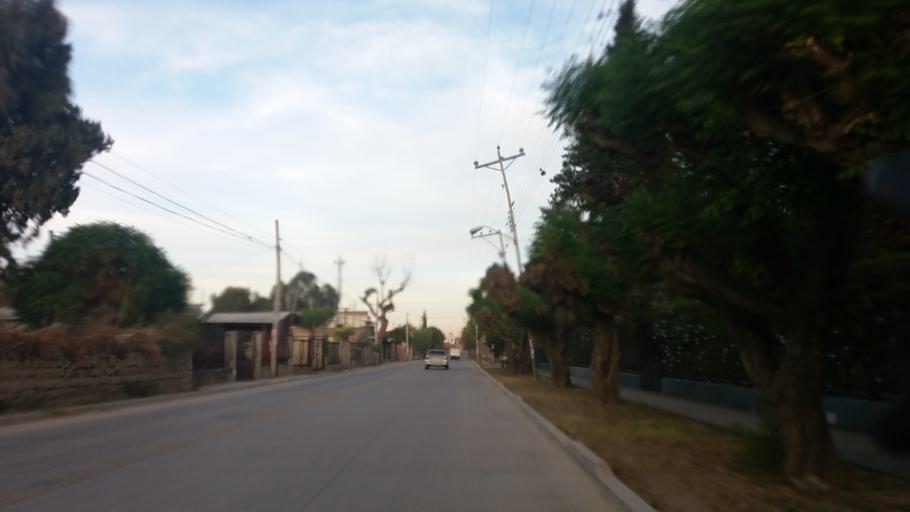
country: BO
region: Cochabamba
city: Cochabamba
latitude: -17.3691
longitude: -66.2092
